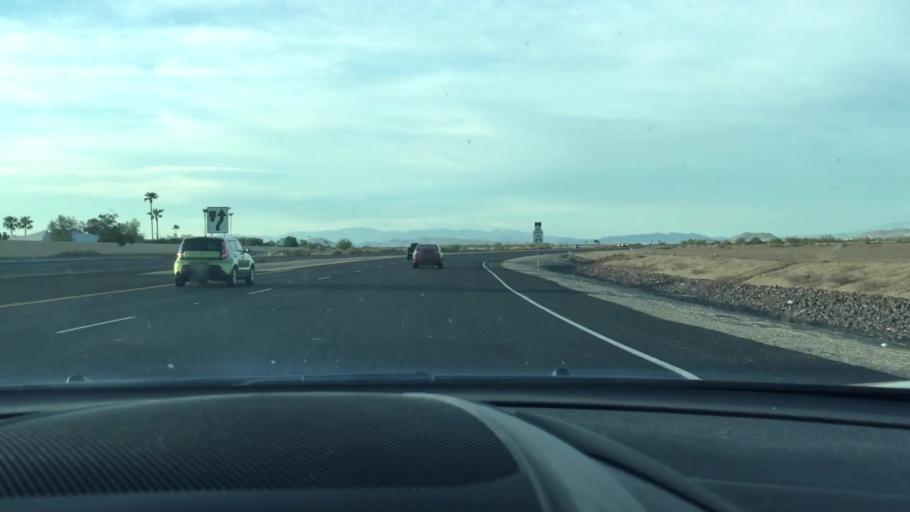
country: US
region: Arizona
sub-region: Maricopa County
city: Surprise
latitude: 33.6402
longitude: -112.3250
